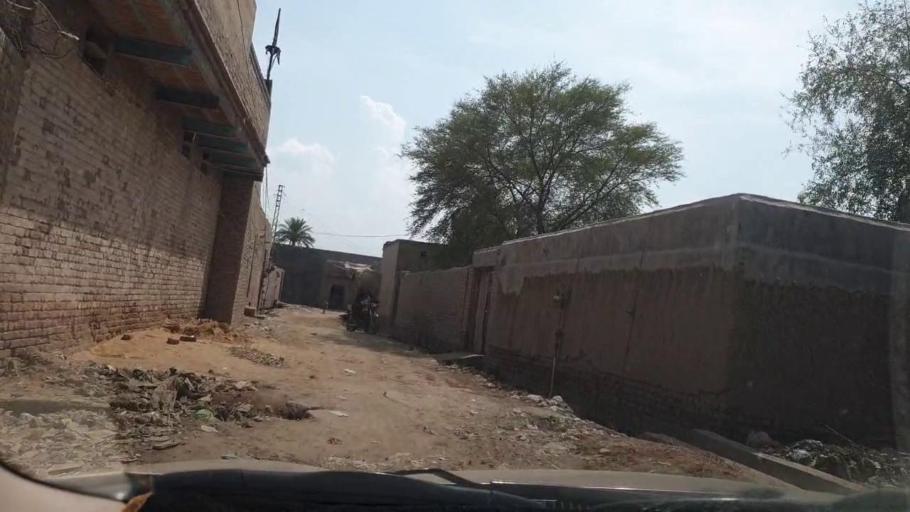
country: PK
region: Sindh
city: Larkana
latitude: 27.5824
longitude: 68.1660
